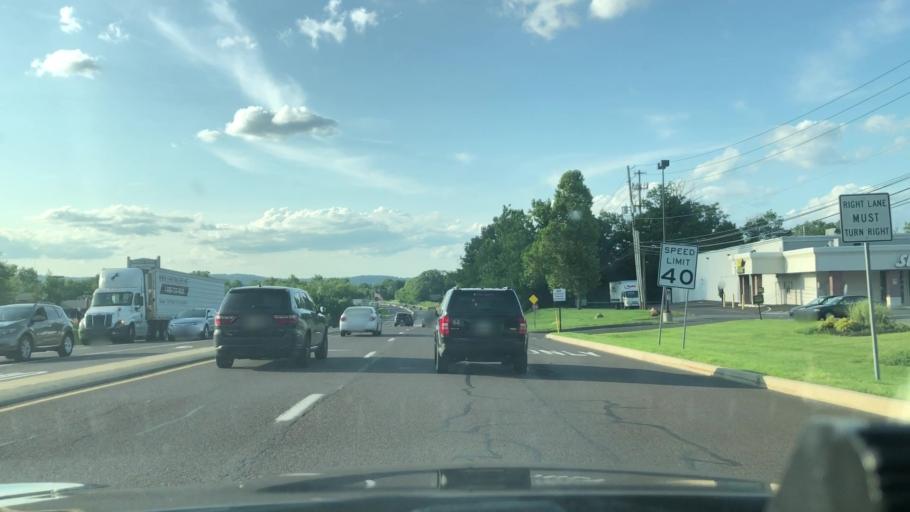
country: US
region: Pennsylvania
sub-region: Lehigh County
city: Coopersburg
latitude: 40.5162
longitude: -75.3853
